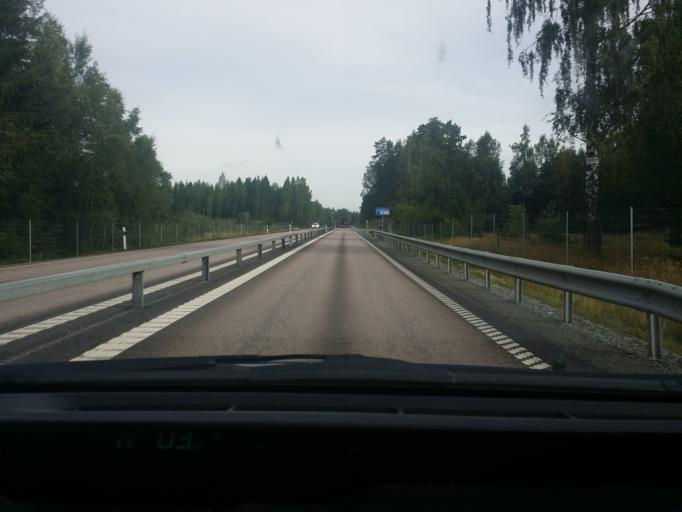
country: SE
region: Vaestmanland
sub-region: Sala Kommun
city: Sala
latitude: 59.8256
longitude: 16.5347
